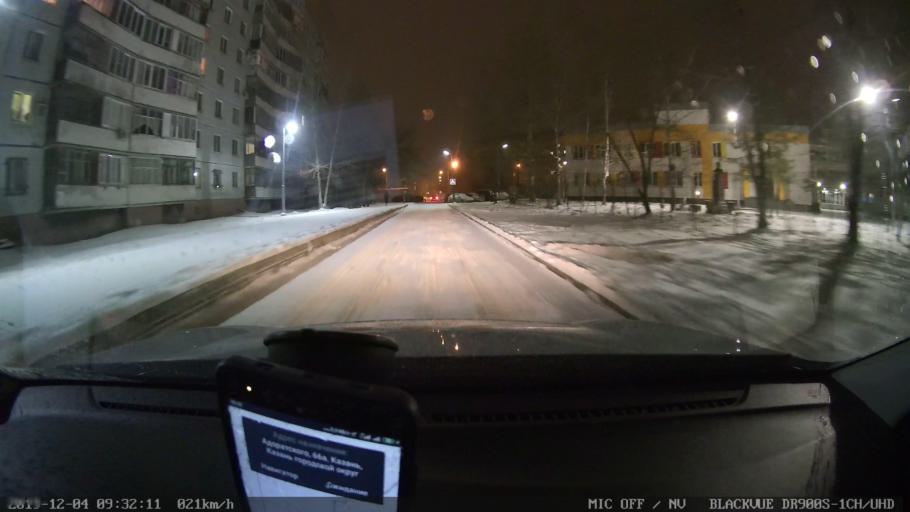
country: RU
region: Tatarstan
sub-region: Gorod Kazan'
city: Kazan
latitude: 55.8397
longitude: 49.1510
